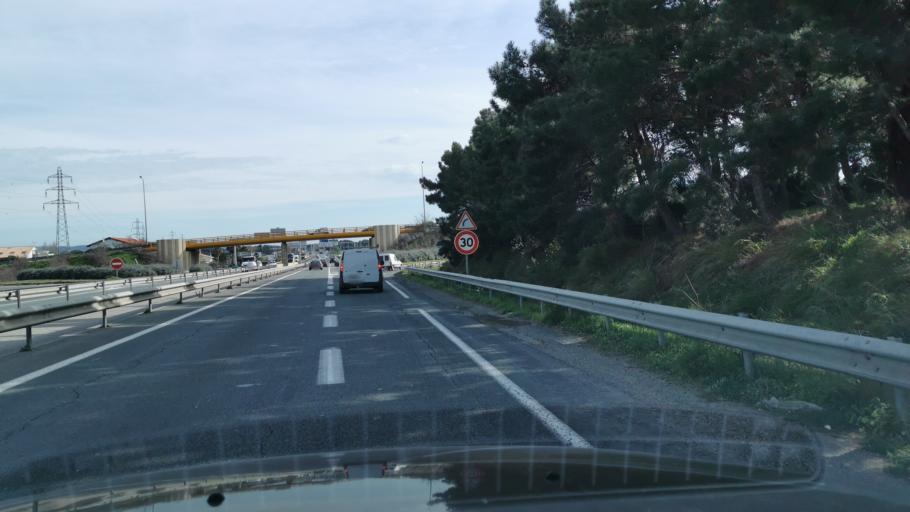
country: FR
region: Languedoc-Roussillon
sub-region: Departement de l'Aude
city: Narbonne
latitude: 43.1692
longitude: 2.9810
